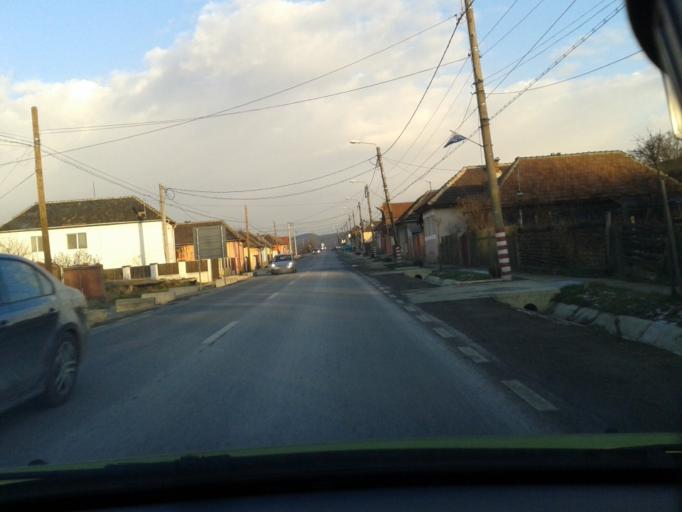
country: RO
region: Sibiu
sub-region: Comuna Copsa Mica
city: Copsa Mica
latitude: 46.1186
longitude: 24.2603
